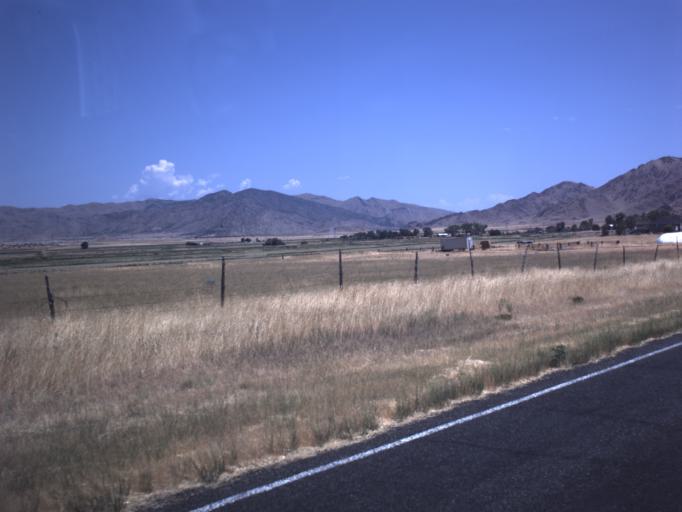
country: US
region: Utah
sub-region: Millard County
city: Delta
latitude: 39.4664
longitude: -112.2793
